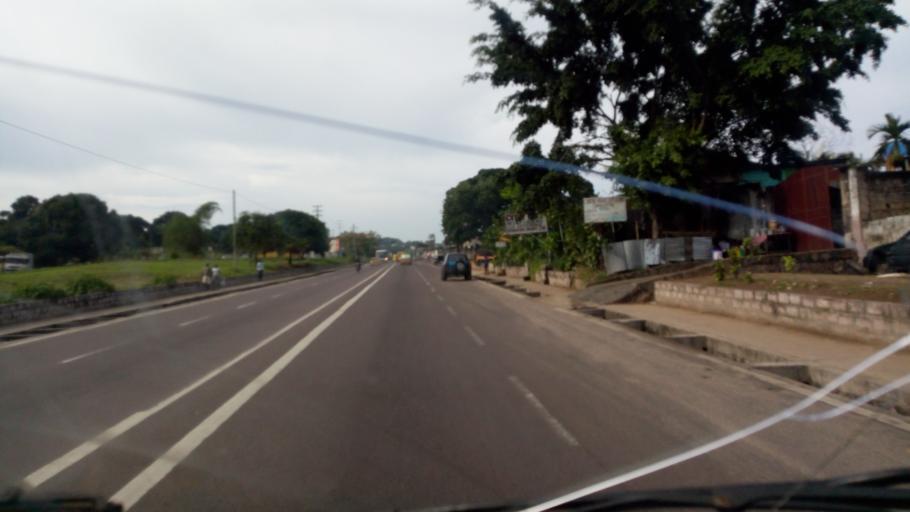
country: CD
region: Kinshasa
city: Kinshasa
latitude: -4.4328
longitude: 15.2580
